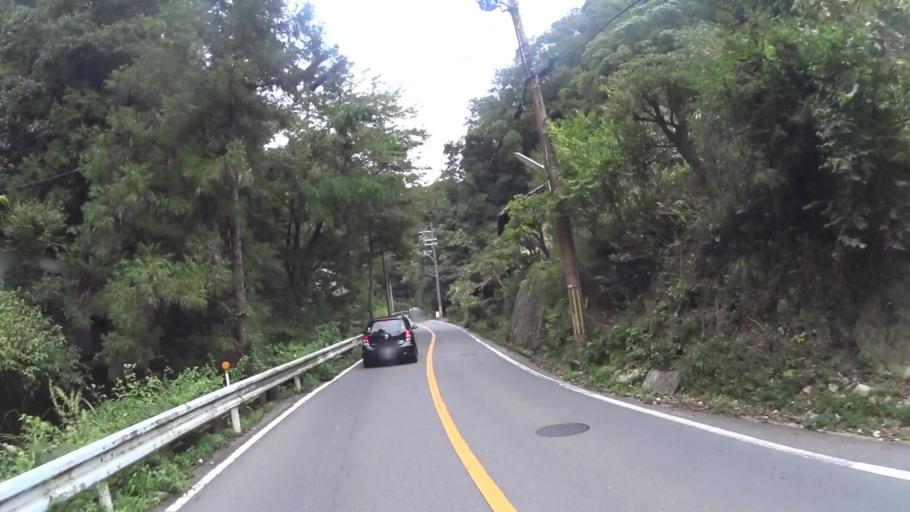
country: JP
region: Kyoto
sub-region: Kyoto-shi
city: Kamigyo-ku
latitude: 35.0347
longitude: 135.8098
